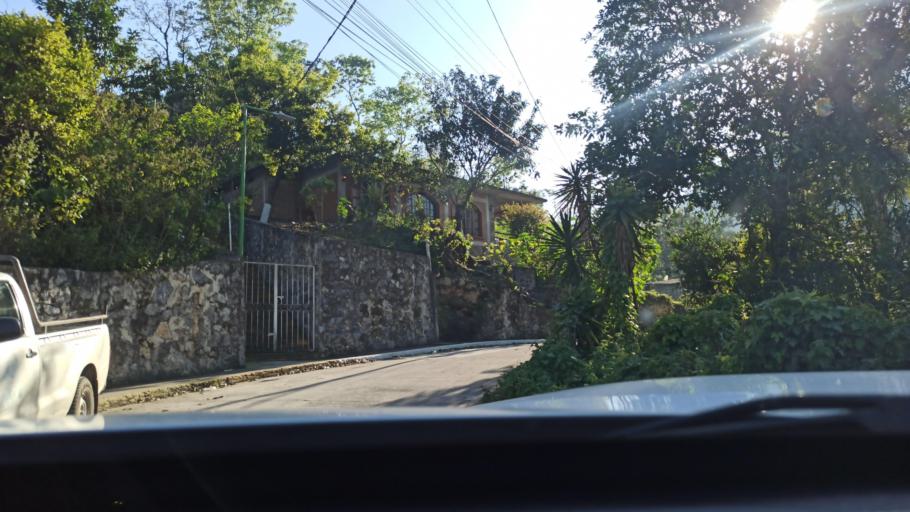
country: MX
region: Veracruz
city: Atzacan
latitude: 18.9058
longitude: -97.0878
